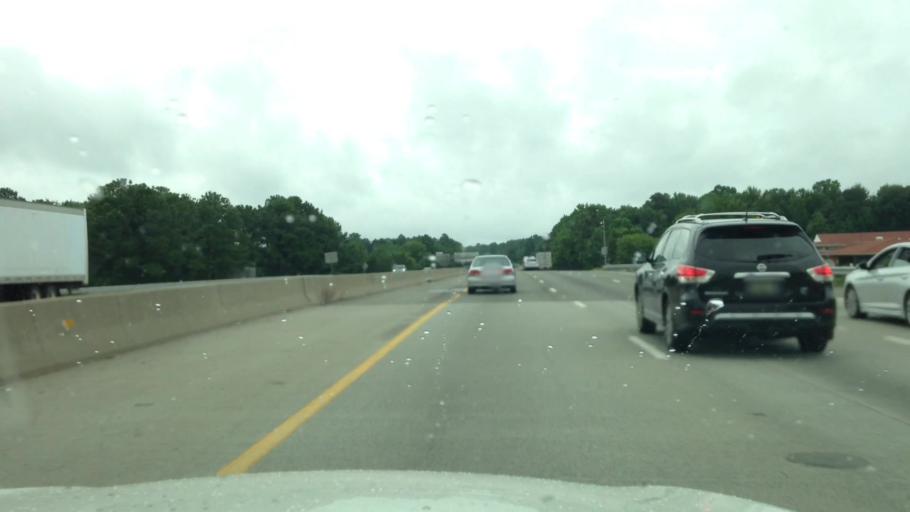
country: US
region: Virginia
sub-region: Chesterfield County
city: Bellwood
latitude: 37.4012
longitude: -77.4247
